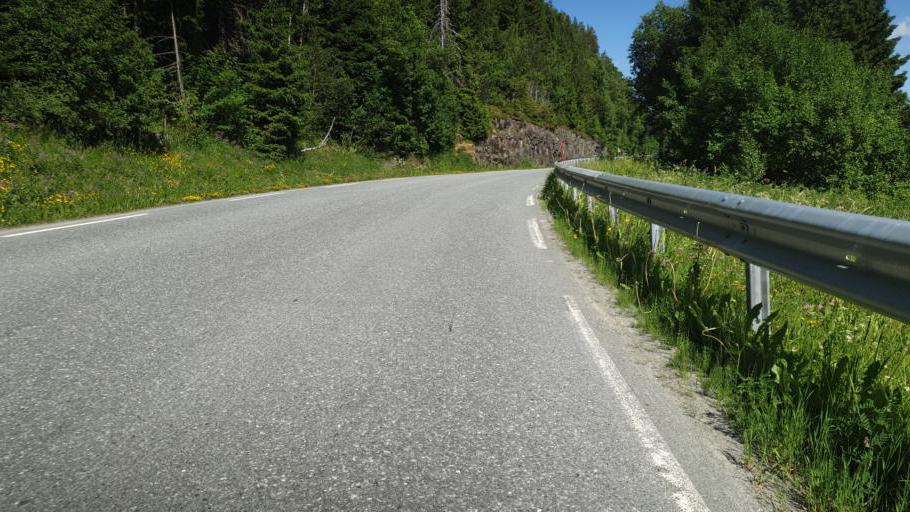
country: NO
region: Nord-Trondelag
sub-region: Leksvik
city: Leksvik
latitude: 63.6004
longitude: 10.4596
